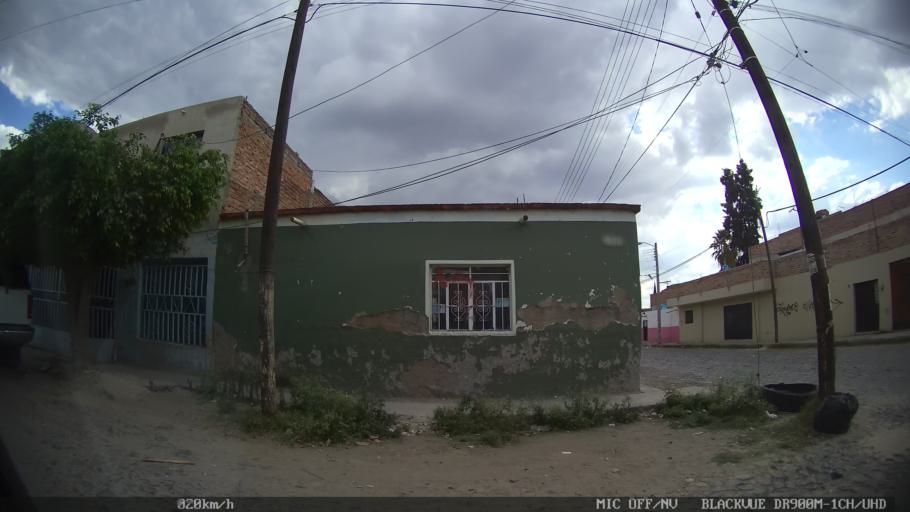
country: MX
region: Jalisco
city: Tonala
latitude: 20.6556
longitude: -103.2553
